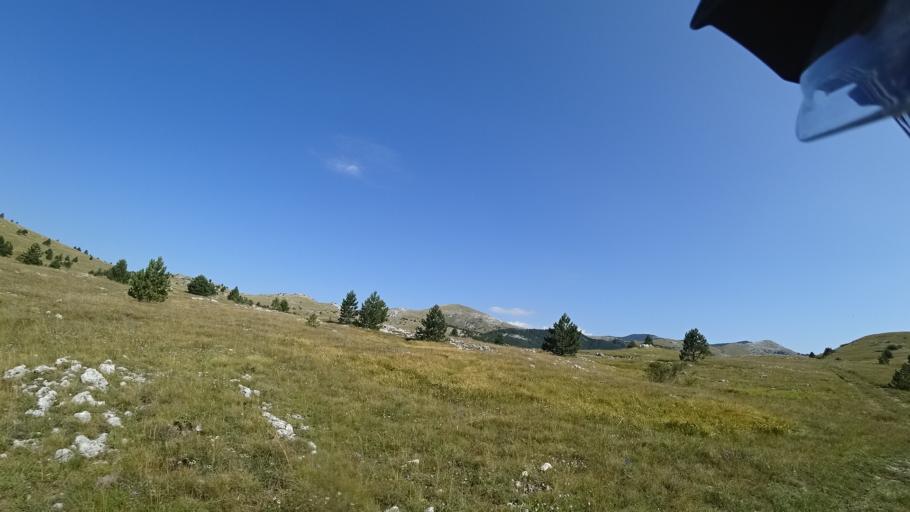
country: HR
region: Zadarska
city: Gracac
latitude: 44.3104
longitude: 15.9965
